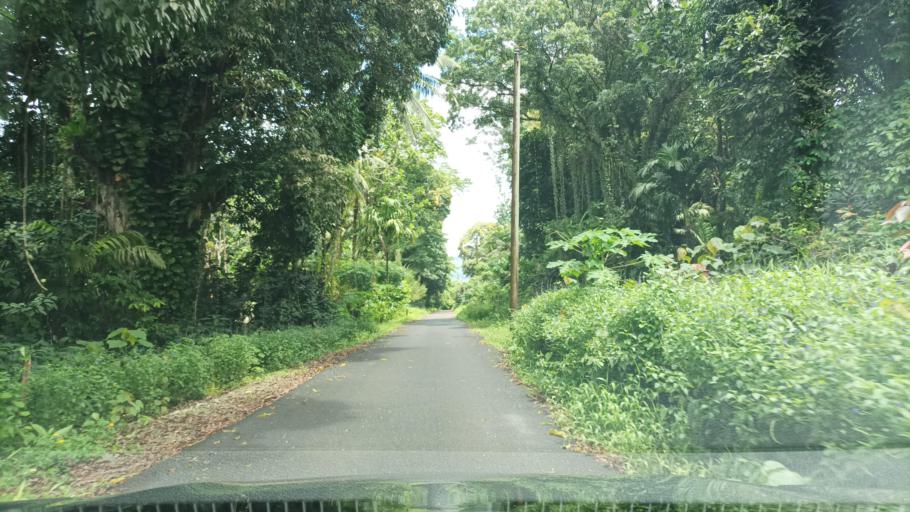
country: FM
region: Pohnpei
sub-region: Kolonia Municipality
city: Kolonia
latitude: 6.9629
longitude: 158.2229
